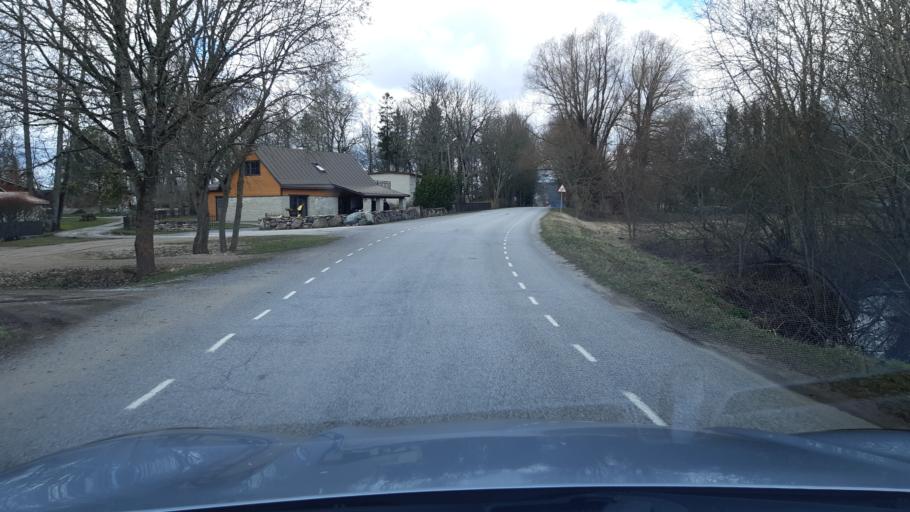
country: EE
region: Raplamaa
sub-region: Kehtna vald
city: Kehtna
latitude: 59.0426
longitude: 25.1194
